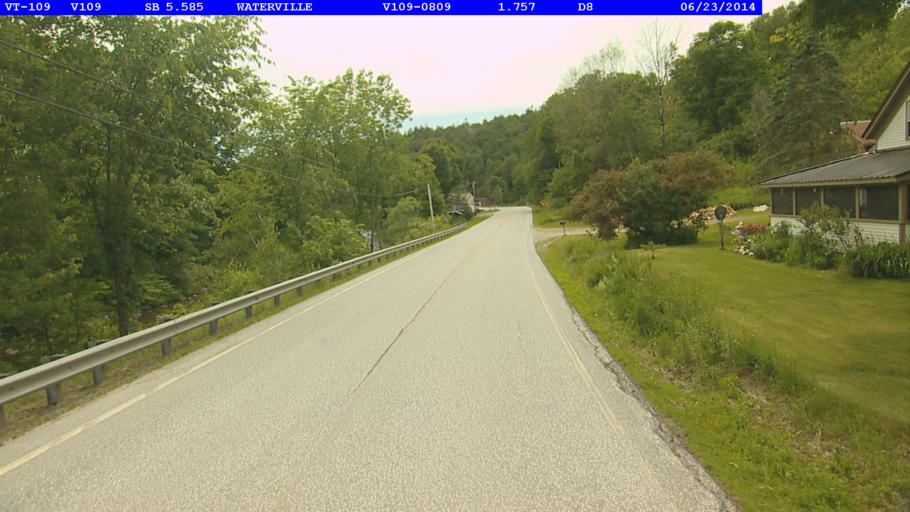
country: US
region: Vermont
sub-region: Lamoille County
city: Johnson
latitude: 44.7055
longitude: -72.7613
